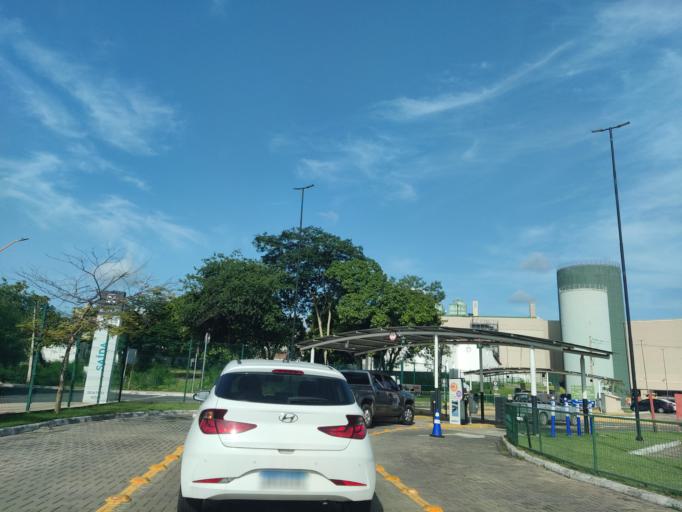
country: BR
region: Piaui
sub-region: Teresina
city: Teresina
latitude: -5.0773
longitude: -42.8035
